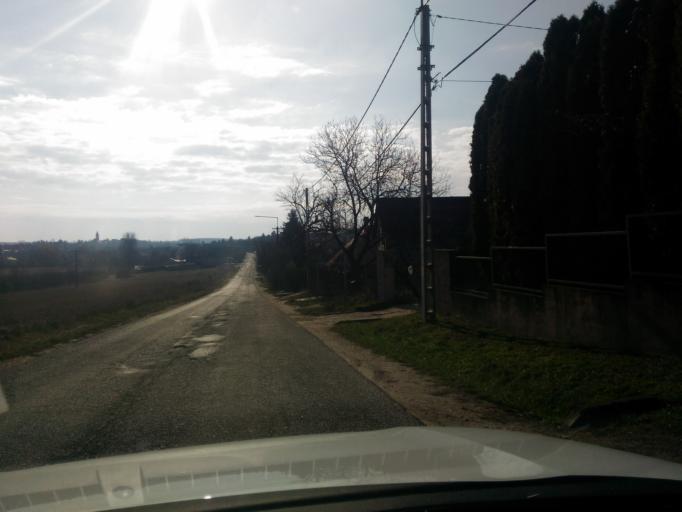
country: HU
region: Fejer
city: Etyek
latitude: 47.4516
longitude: 18.7376
